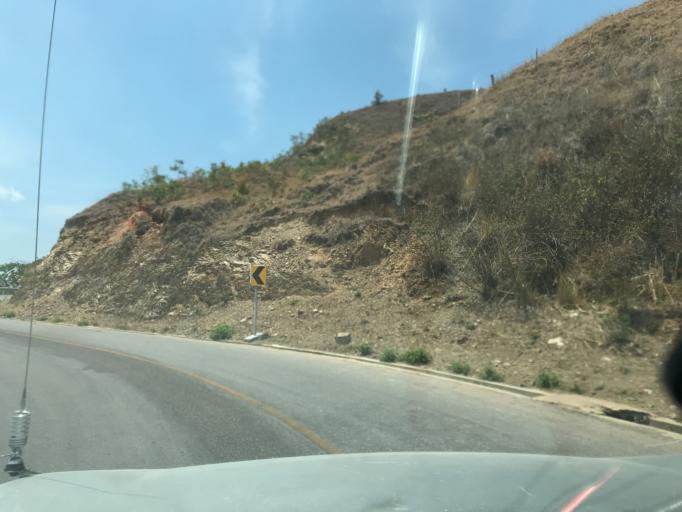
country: TL
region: Aileu
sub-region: Aileu Villa
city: Aileu
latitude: -8.8076
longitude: 125.5966
